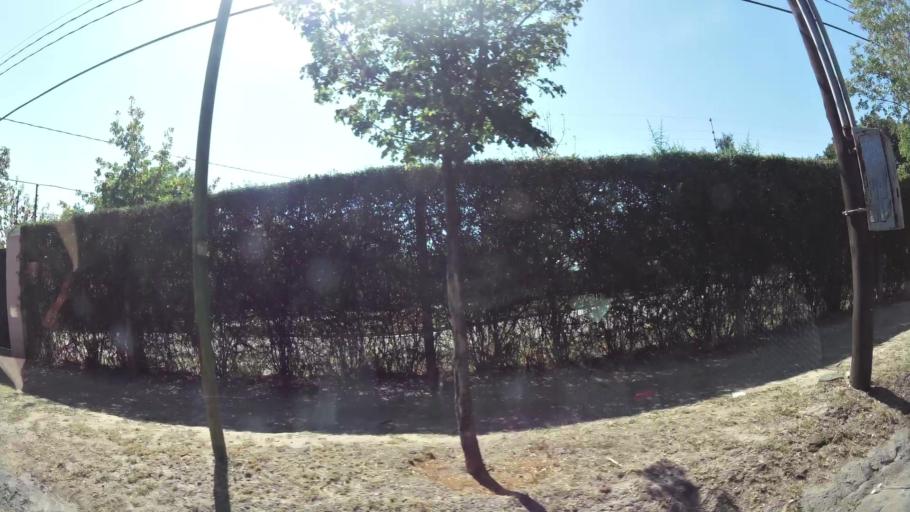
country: AR
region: Cordoba
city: Villa Allende
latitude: -31.2975
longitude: -64.2795
